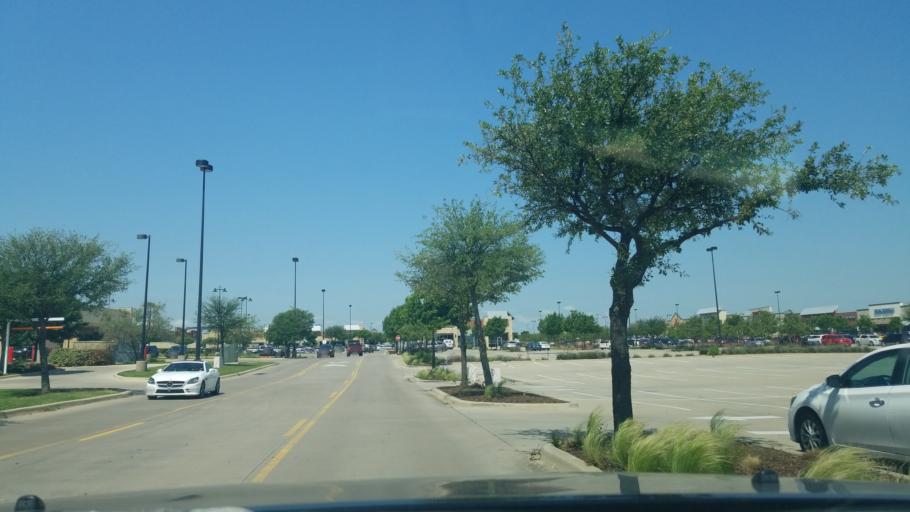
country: US
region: Texas
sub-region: Denton County
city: Denton
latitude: 33.2308
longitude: -97.1635
